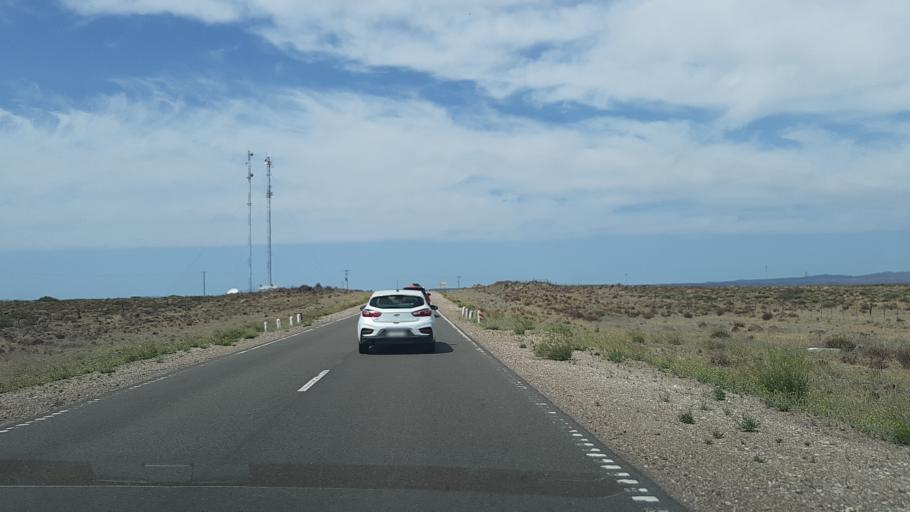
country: AR
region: Neuquen
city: Piedra del Aguila
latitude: -39.9956
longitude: -70.0420
